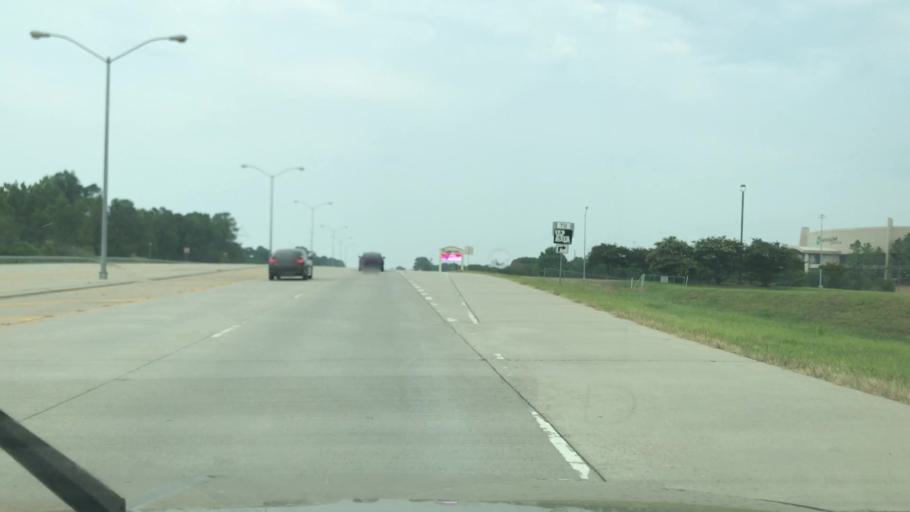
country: US
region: Louisiana
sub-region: Bossier Parish
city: Bossier City
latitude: 32.4612
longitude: -93.6756
